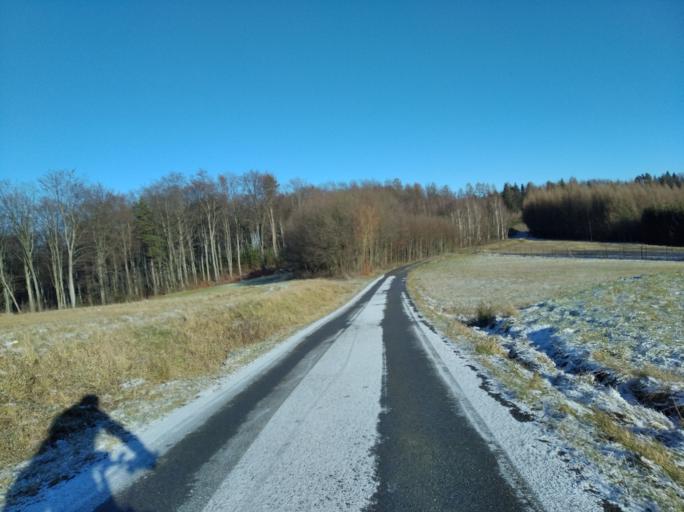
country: PL
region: Subcarpathian Voivodeship
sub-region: Powiat ropczycko-sedziszowski
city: Iwierzyce
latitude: 49.9678
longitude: 21.7253
